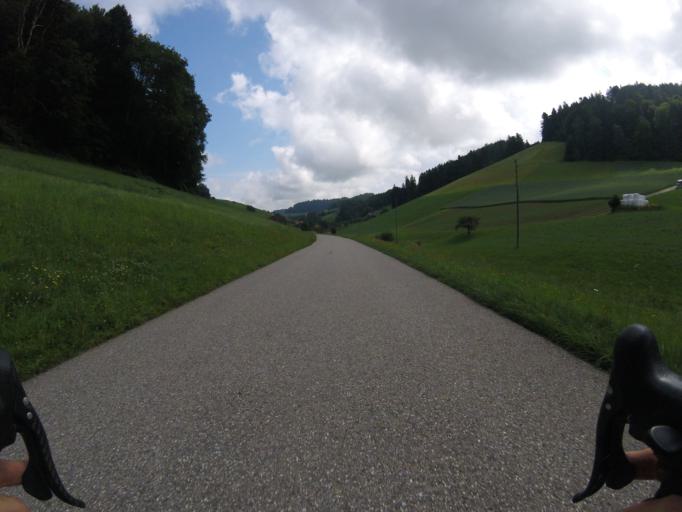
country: CH
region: Bern
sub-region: Emmental District
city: Krauchthal
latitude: 46.9960
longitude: 7.5883
